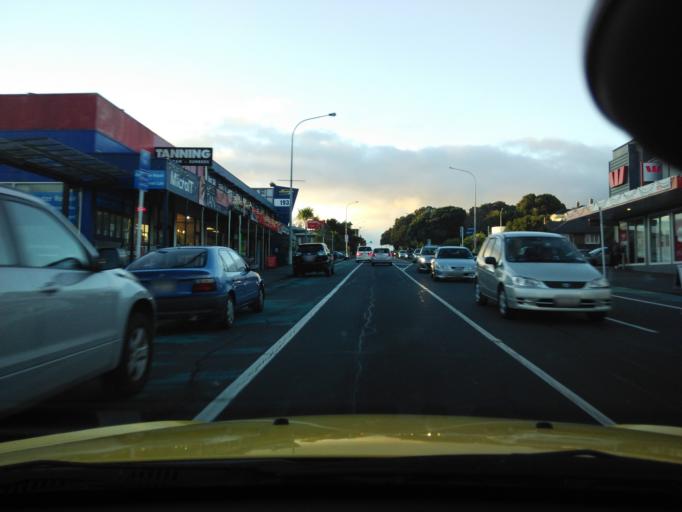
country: NZ
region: Auckland
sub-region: Auckland
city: Auckland
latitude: -36.8754
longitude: 174.7510
